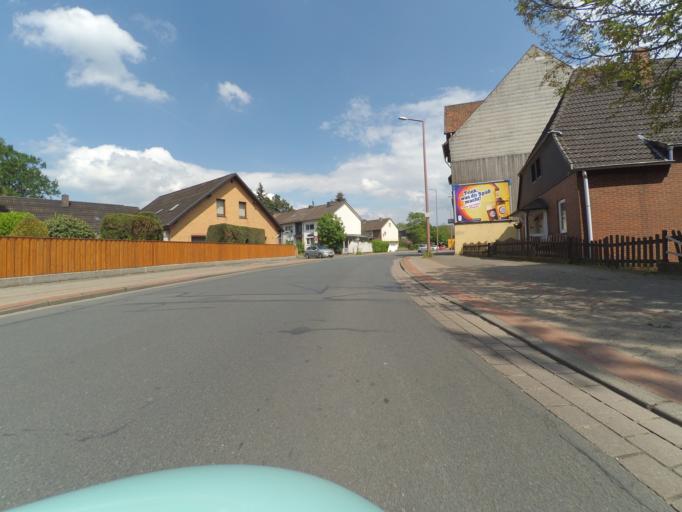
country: DE
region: Lower Saxony
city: Lehrte
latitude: 52.3703
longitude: 9.9733
